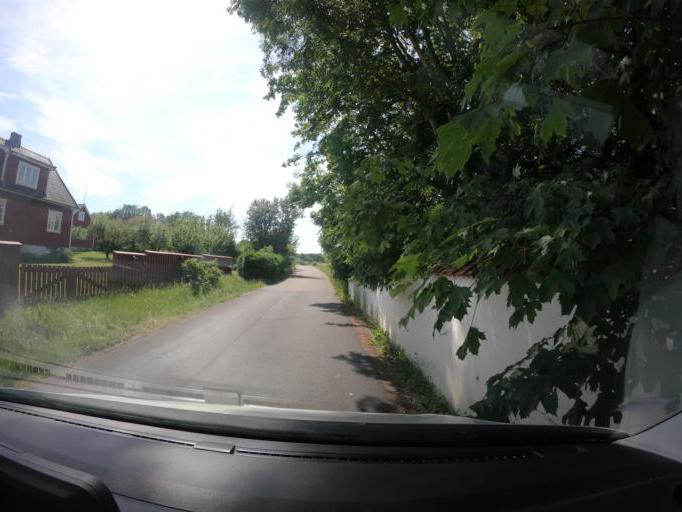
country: SE
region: Skane
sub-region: Bastads Kommun
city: Bastad
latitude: 56.4660
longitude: 12.7081
